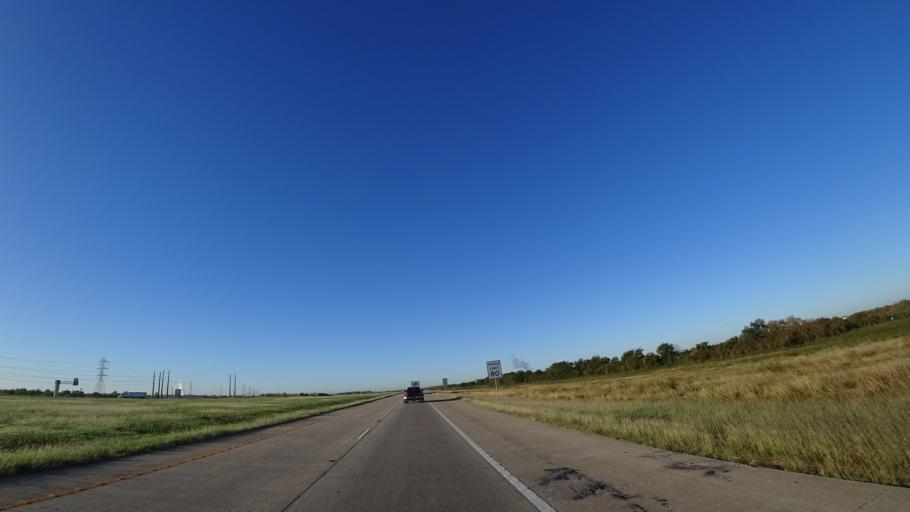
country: US
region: Texas
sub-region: Travis County
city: Hornsby Bend
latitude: 30.2411
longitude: -97.6144
